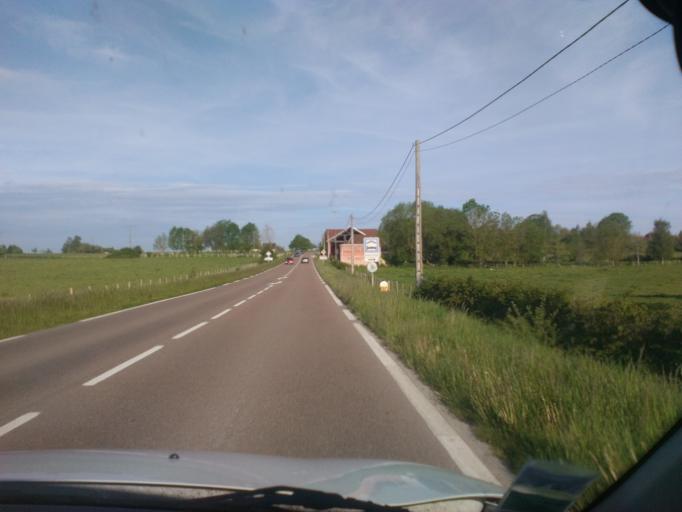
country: FR
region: Champagne-Ardenne
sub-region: Departement de l'Aube
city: Vendeuvre-sur-Barse
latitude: 48.2356
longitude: 4.3929
